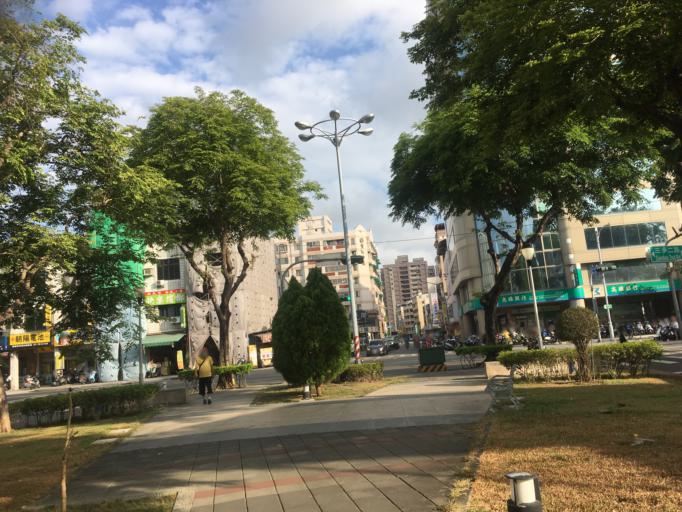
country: TW
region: Kaohsiung
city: Kaohsiung
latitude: 22.6204
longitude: 120.3232
